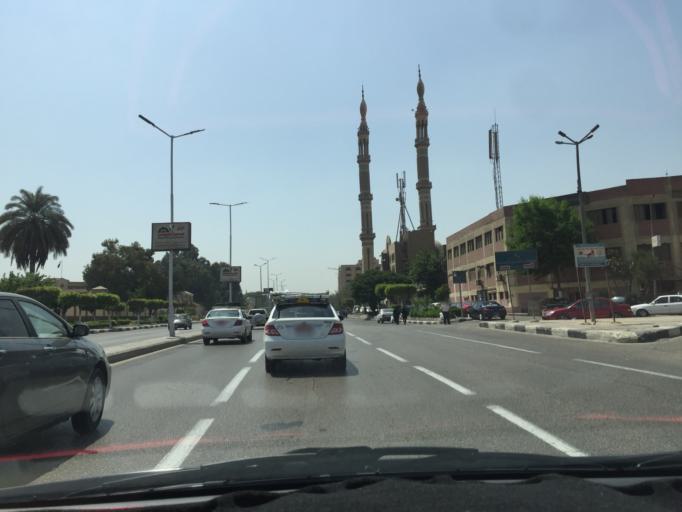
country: EG
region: Muhafazat al Qahirah
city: Cairo
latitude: 30.0627
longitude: 31.2854
